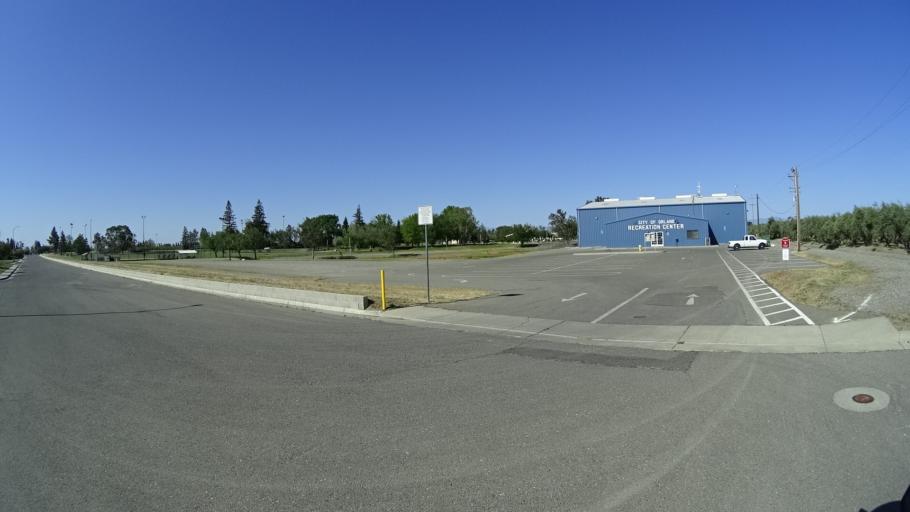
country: US
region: California
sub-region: Glenn County
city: Orland
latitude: 39.7397
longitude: -122.1687
